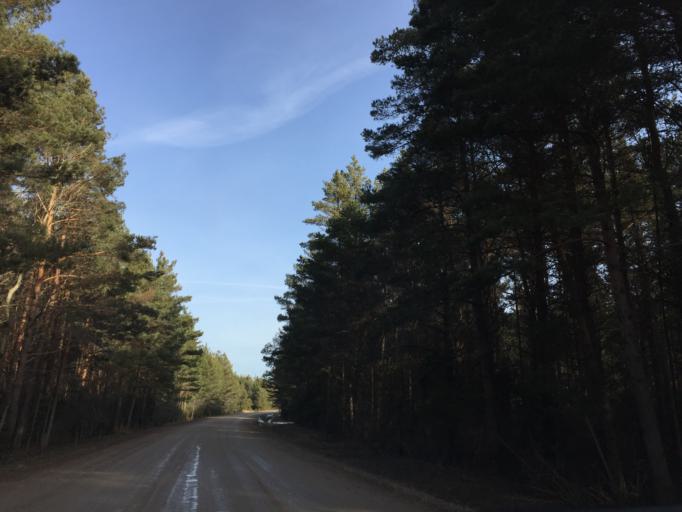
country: EE
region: Saare
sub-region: Kuressaare linn
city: Kuressaare
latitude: 58.2798
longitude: 21.9172
